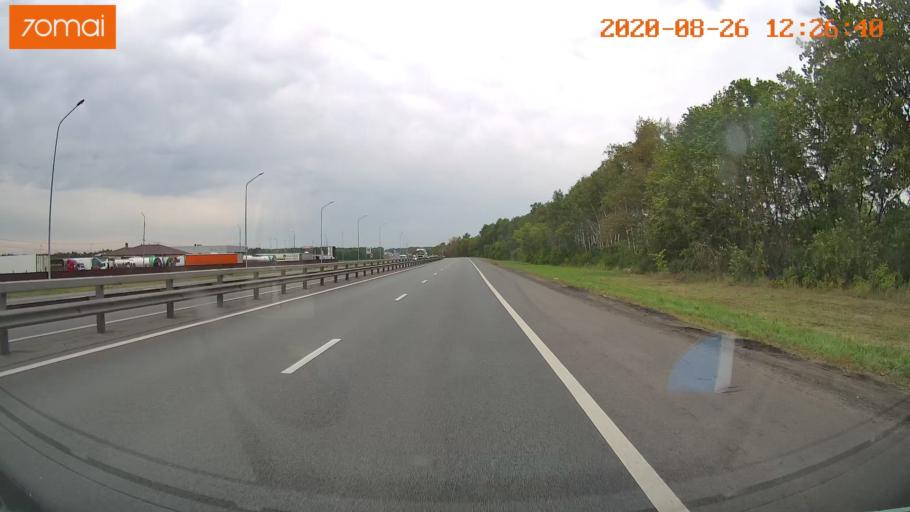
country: RU
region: Rjazan
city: Polyany
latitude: 54.5369
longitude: 39.8554
